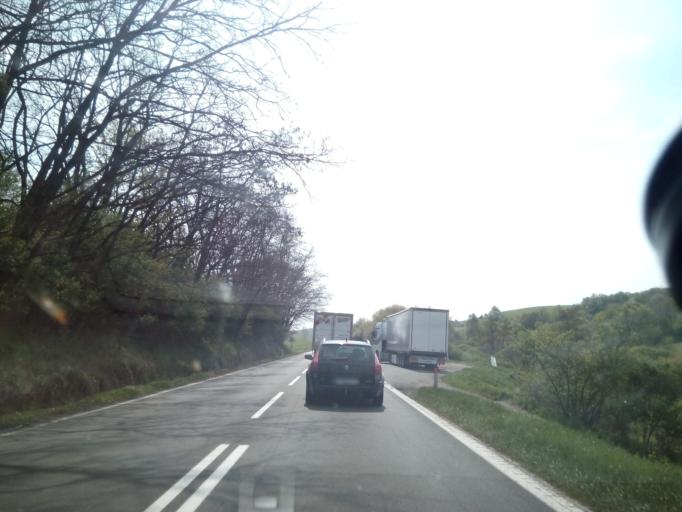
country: SK
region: Presovsky
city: Giraltovce
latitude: 49.0443
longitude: 21.4418
